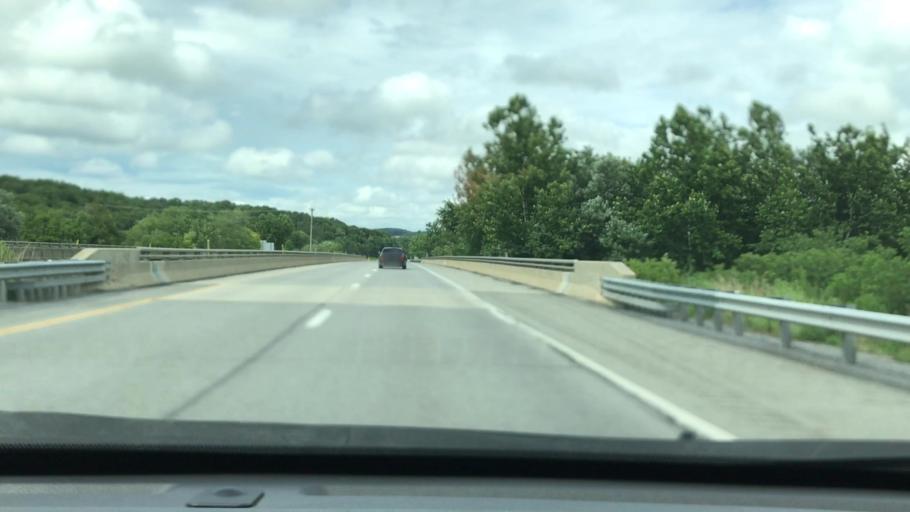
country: US
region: Pennsylvania
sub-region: Bedford County
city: Bedford
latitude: 40.1014
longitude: -78.5284
